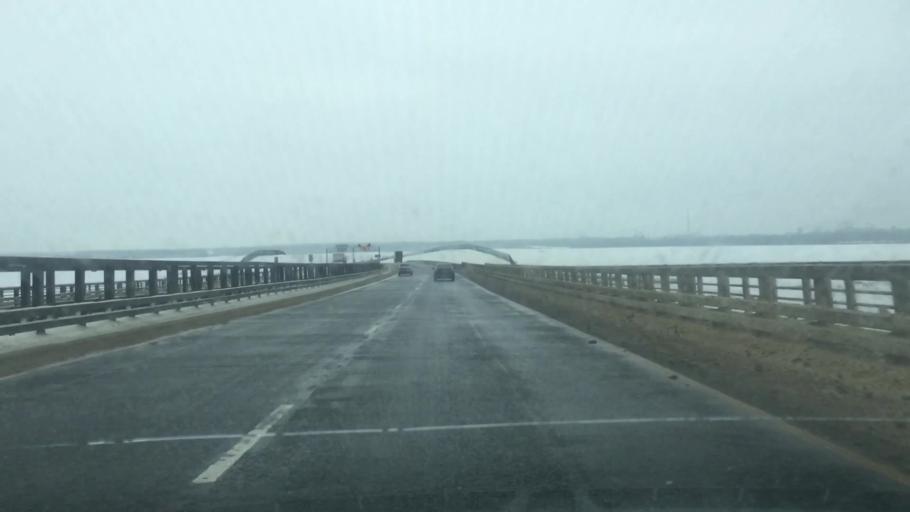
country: RU
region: Tula
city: Yefremov
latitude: 53.1145
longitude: 38.1964
